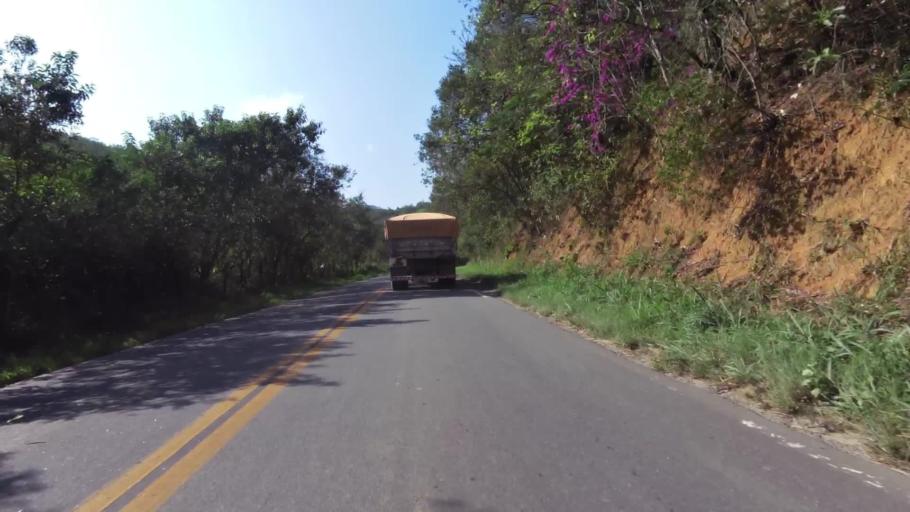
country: BR
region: Espirito Santo
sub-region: Rio Novo Do Sul
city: Rio Novo do Sul
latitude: -20.8791
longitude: -40.9071
